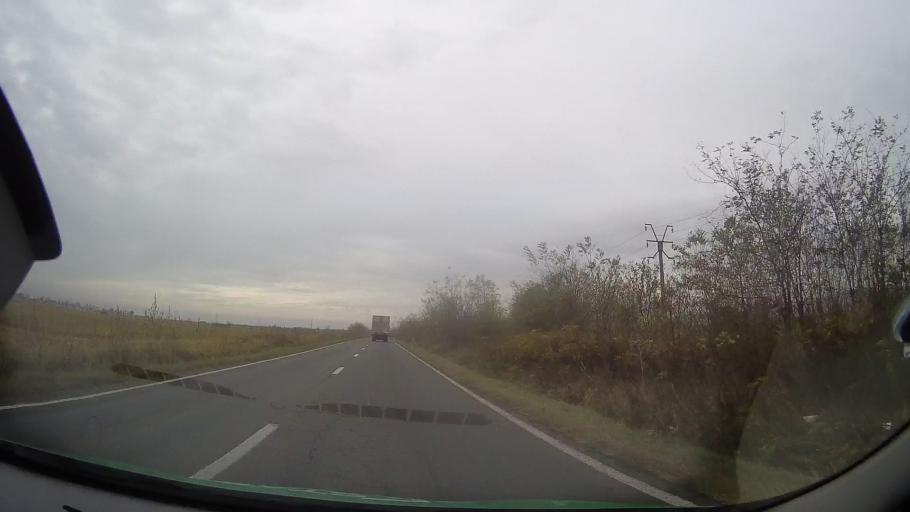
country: RO
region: Prahova
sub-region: Oras Urlati
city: Urlati
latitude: 44.9584
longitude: 26.2489
